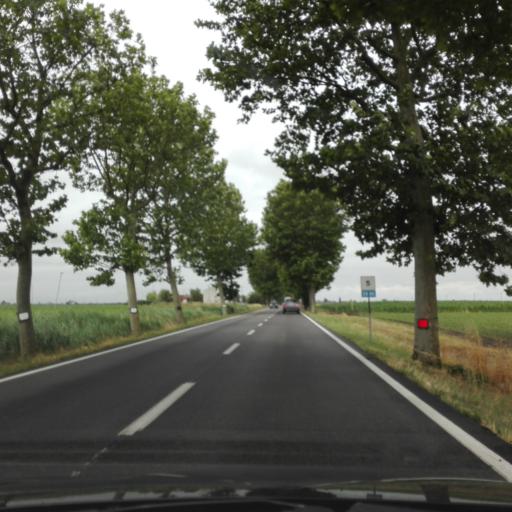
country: IT
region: Veneto
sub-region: Provincia di Padova
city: Barbona
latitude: 45.0773
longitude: 11.7036
